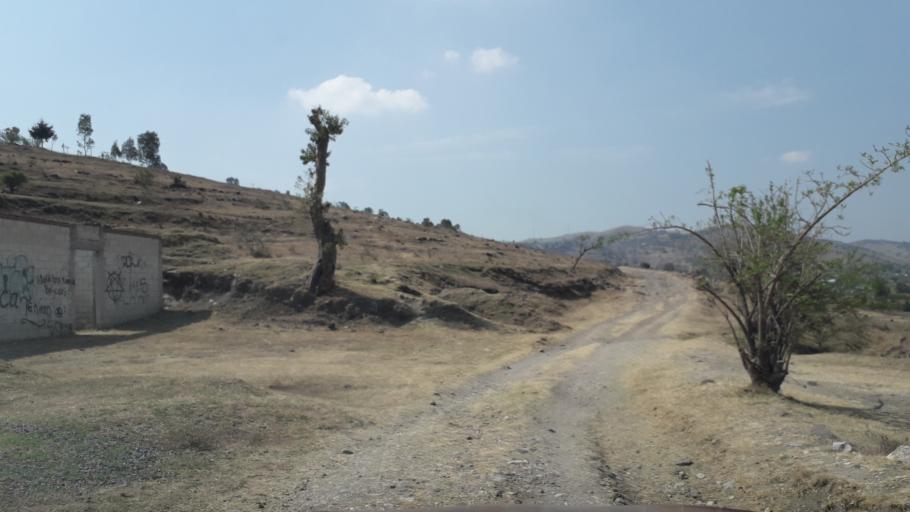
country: MX
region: Puebla
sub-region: Puebla
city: San Andres Azumiatla
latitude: 18.9108
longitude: -98.2594
